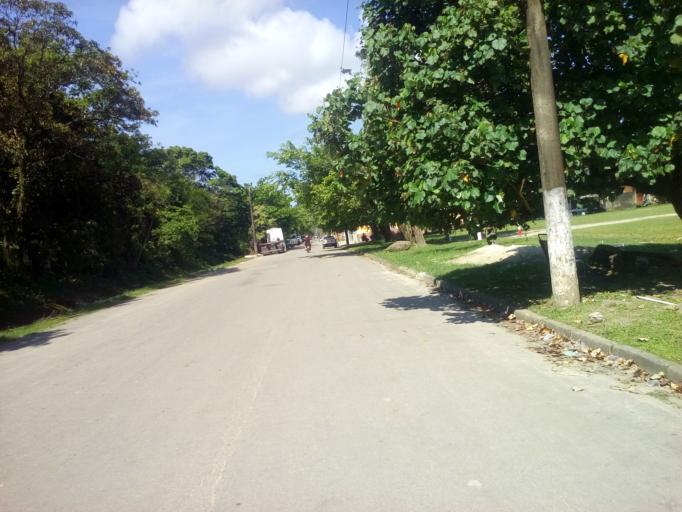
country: BR
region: Sao Paulo
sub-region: Guaruja
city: Guaruja
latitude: -23.9627
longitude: -46.2591
